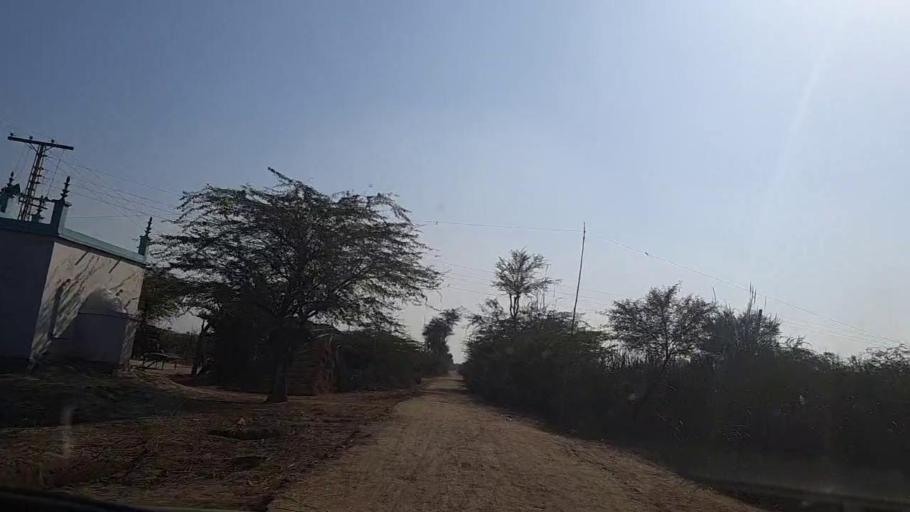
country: PK
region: Sindh
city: Sakrand
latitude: 26.0825
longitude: 68.3695
